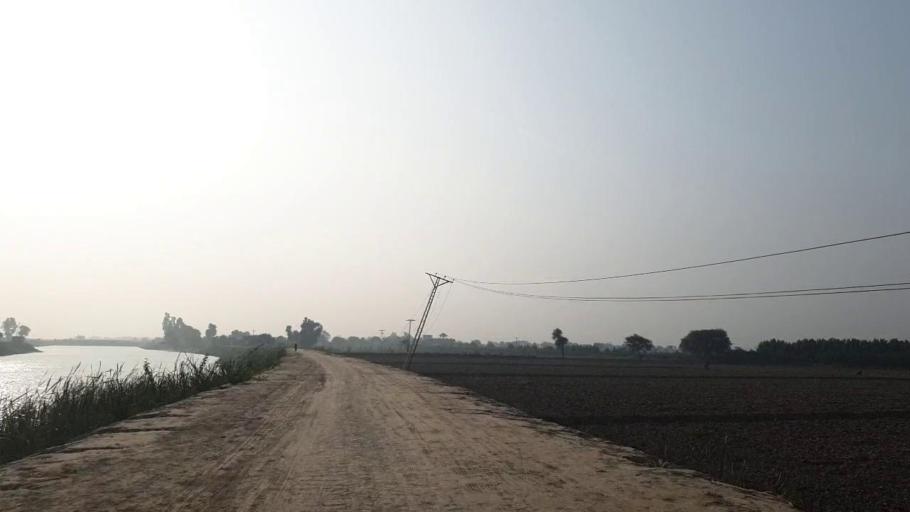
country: PK
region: Sindh
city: Tando Muhammad Khan
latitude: 25.0943
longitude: 68.5779
